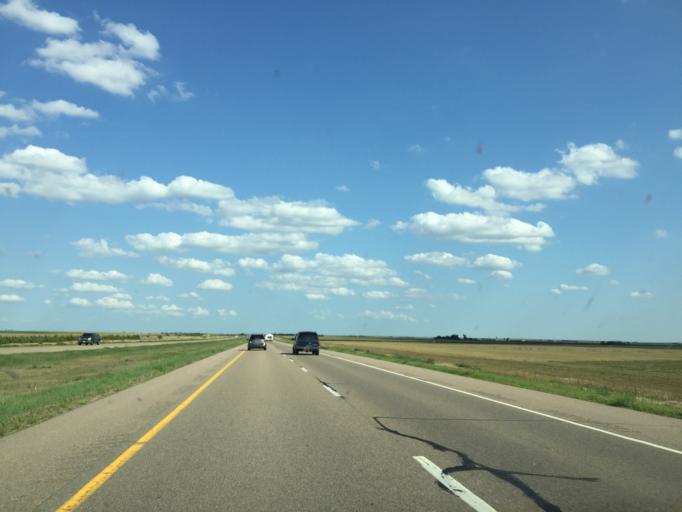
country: US
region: Kansas
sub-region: Gove County
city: Gove
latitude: 39.0402
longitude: -100.2042
